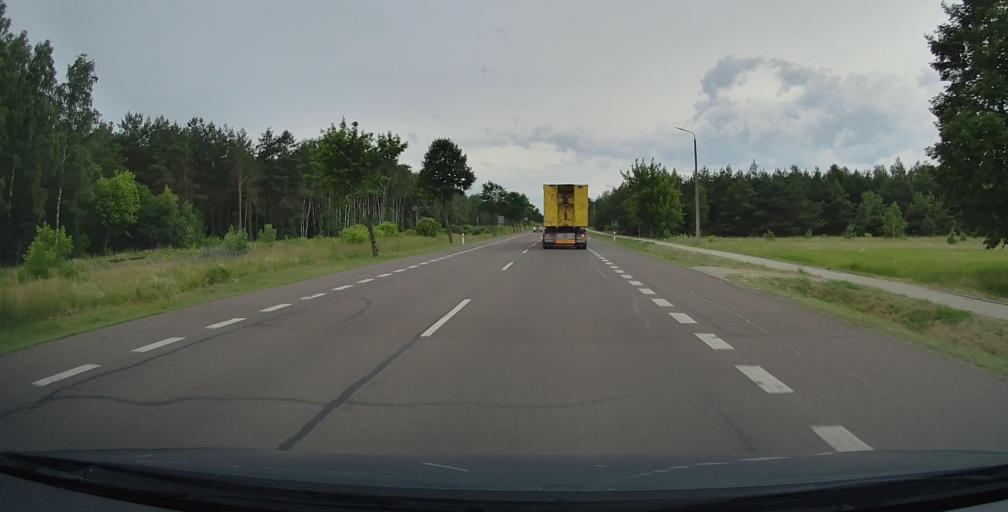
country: PL
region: Lublin Voivodeship
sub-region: Powiat bialski
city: Terespol
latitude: 52.0427
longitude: 23.5309
